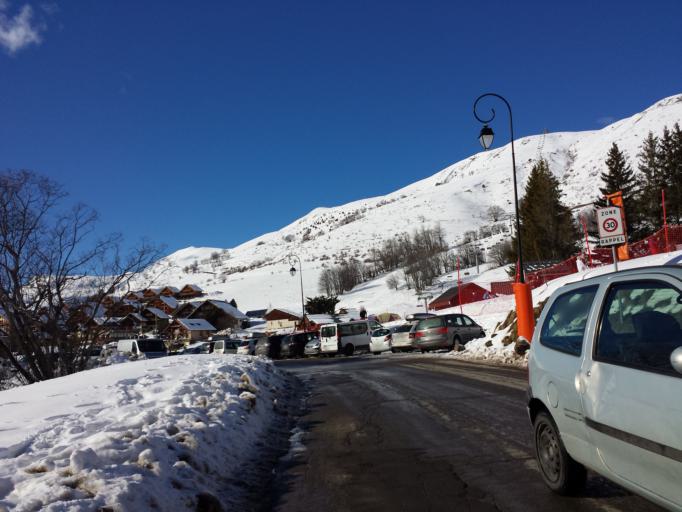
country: FR
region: Rhone-Alpes
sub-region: Departement de la Savoie
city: Saint-Jean-de-Maurienne
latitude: 45.2127
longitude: 6.2680
